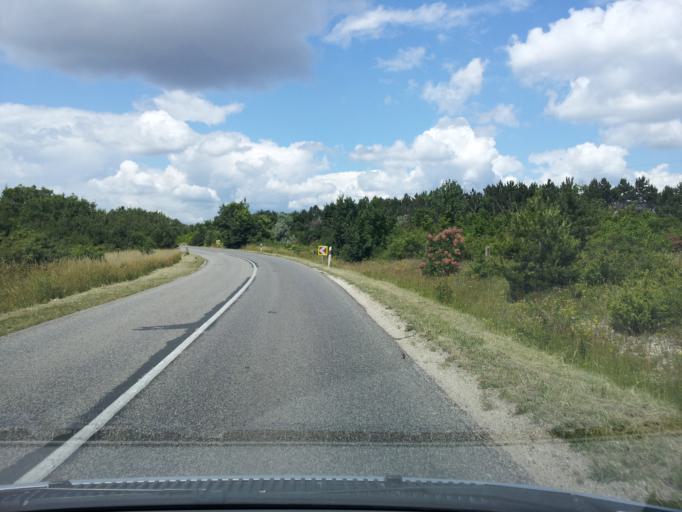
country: HU
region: Veszprem
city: Szentkiralyszabadja
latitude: 47.0618
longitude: 17.9728
